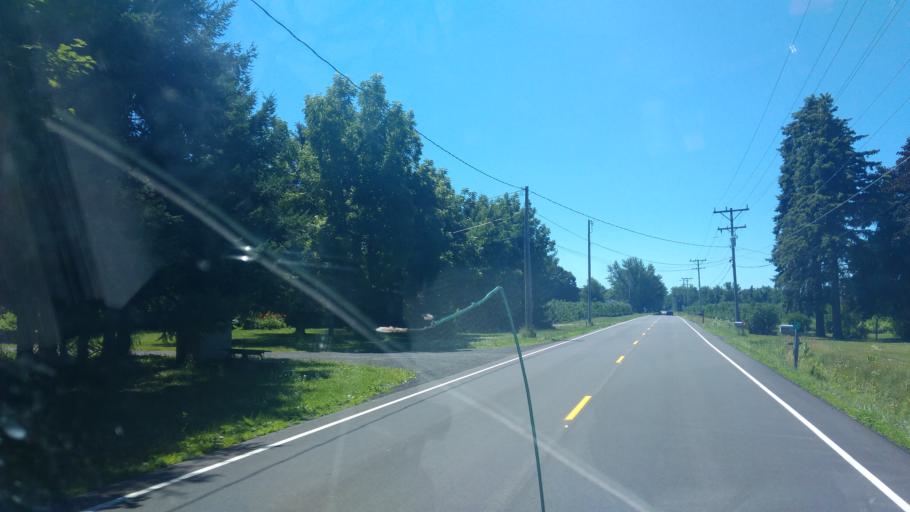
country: US
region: New York
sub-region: Wayne County
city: Sodus
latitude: 43.2192
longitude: -76.9821
